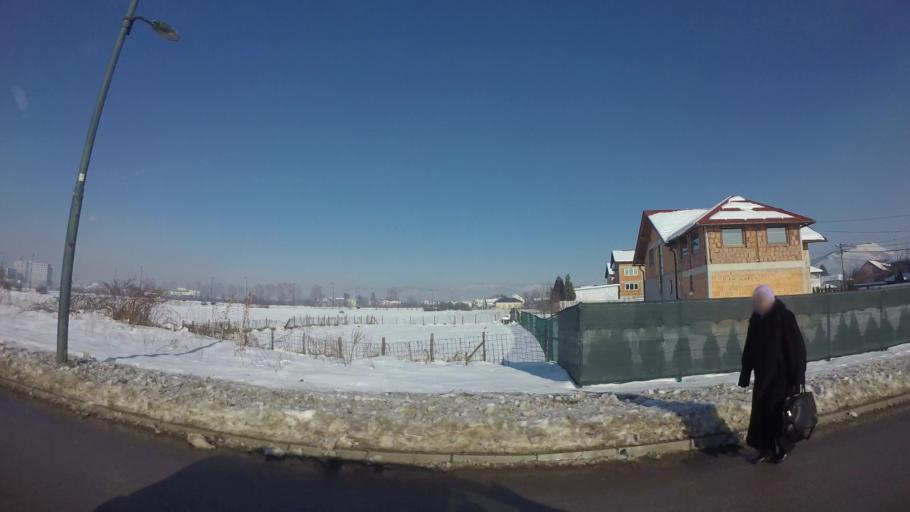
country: BA
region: Federation of Bosnia and Herzegovina
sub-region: Kanton Sarajevo
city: Sarajevo
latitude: 43.8197
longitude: 18.3167
